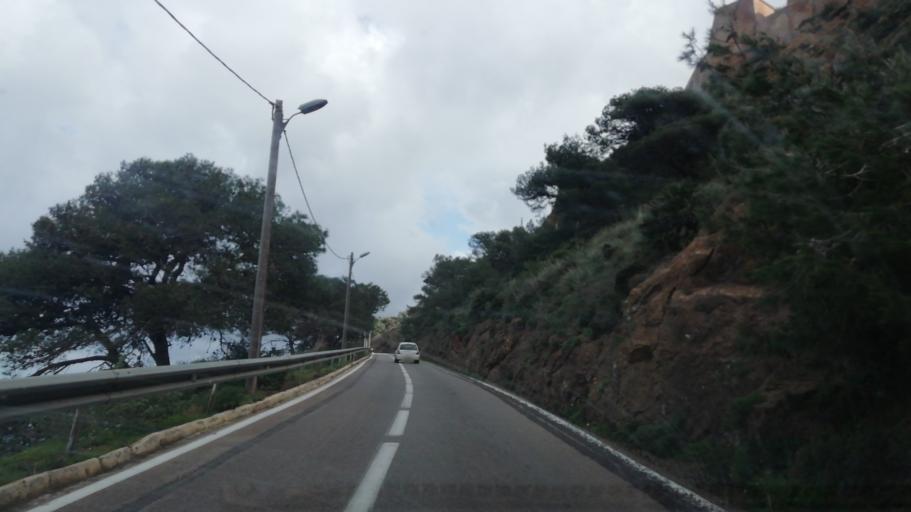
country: DZ
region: Oran
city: Oran
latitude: 35.7093
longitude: -0.6669
